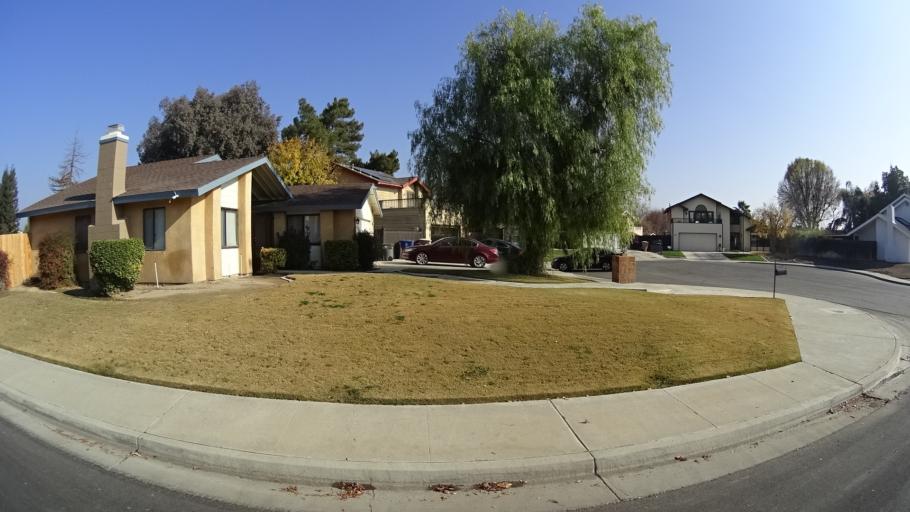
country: US
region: California
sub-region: Kern County
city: Greenacres
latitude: 35.3221
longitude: -119.0867
